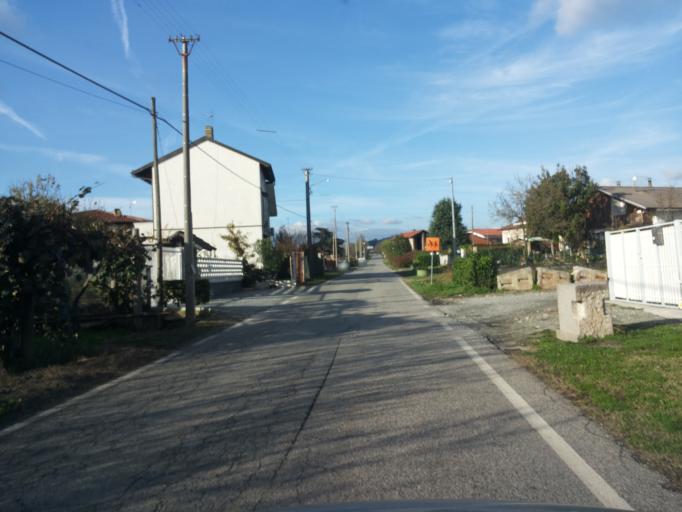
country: IT
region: Piedmont
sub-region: Provincia di Vercelli
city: Alice Castello
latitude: 45.3744
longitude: 8.0731
